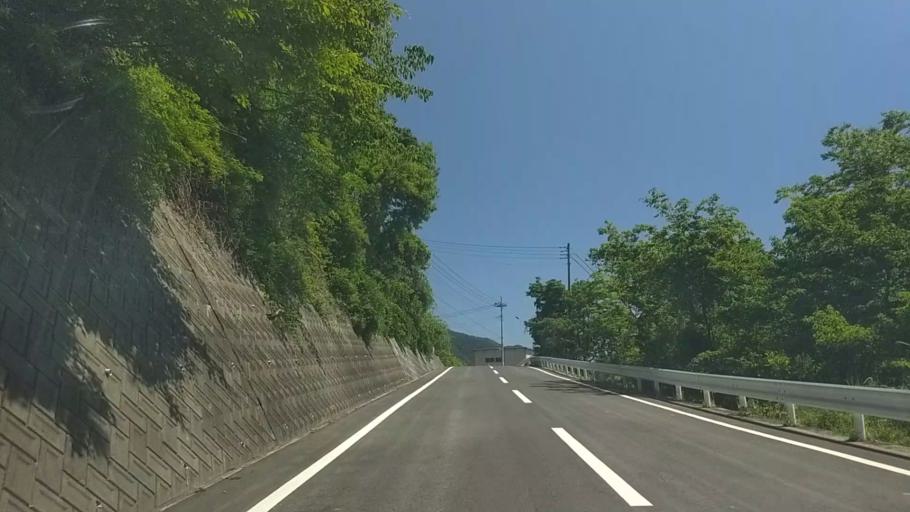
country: JP
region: Yamanashi
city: Nirasaki
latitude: 35.8508
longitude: 138.4387
